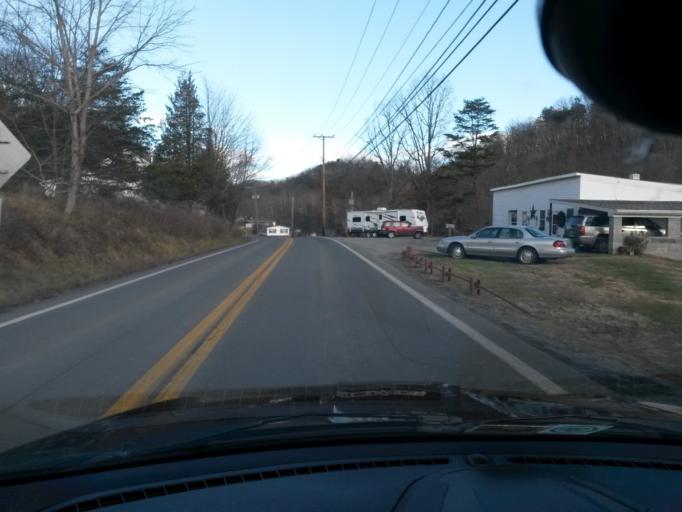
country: US
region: Virginia
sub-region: Giles County
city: Narrows
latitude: 37.3953
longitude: -80.7813
